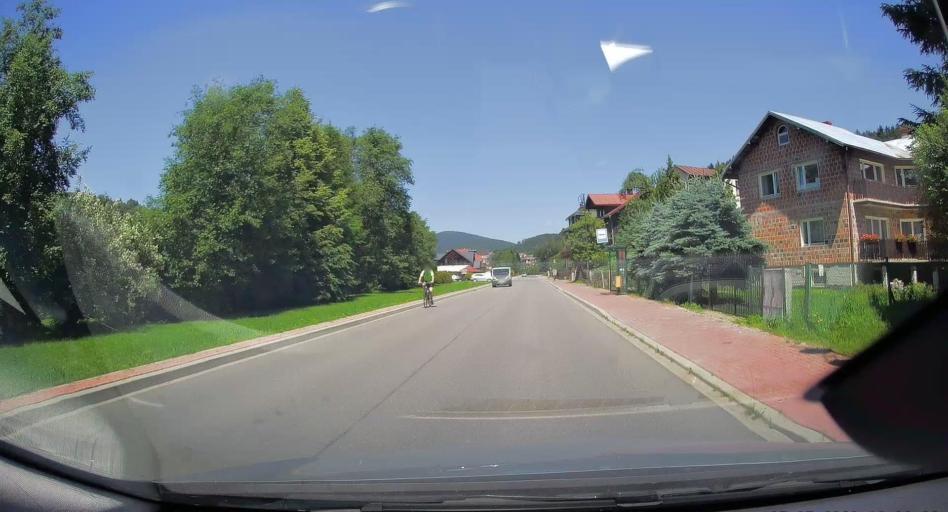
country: PL
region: Lesser Poland Voivodeship
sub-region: Powiat nowosadecki
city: Muszyna
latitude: 49.3571
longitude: 20.8886
